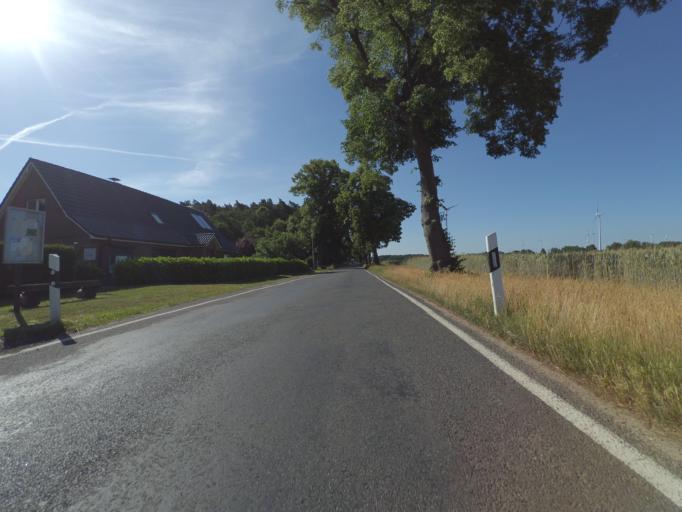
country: DE
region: Brandenburg
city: Putlitz
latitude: 53.3424
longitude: 12.0425
